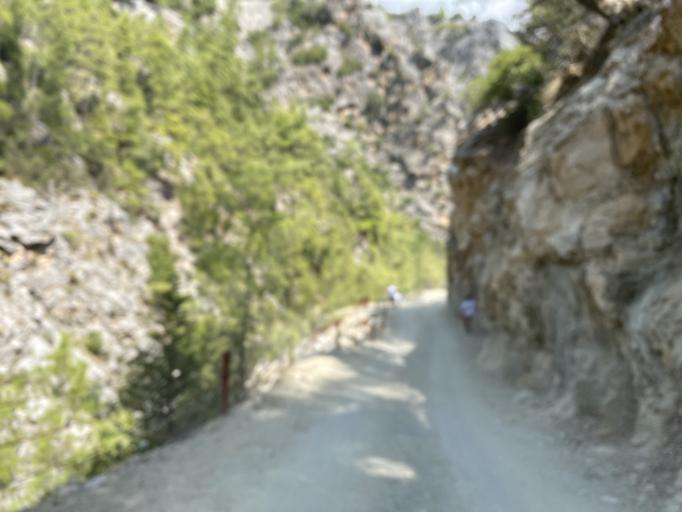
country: TR
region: Antalya
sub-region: Kemer
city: Goeynuek
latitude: 36.6804
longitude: 30.5192
